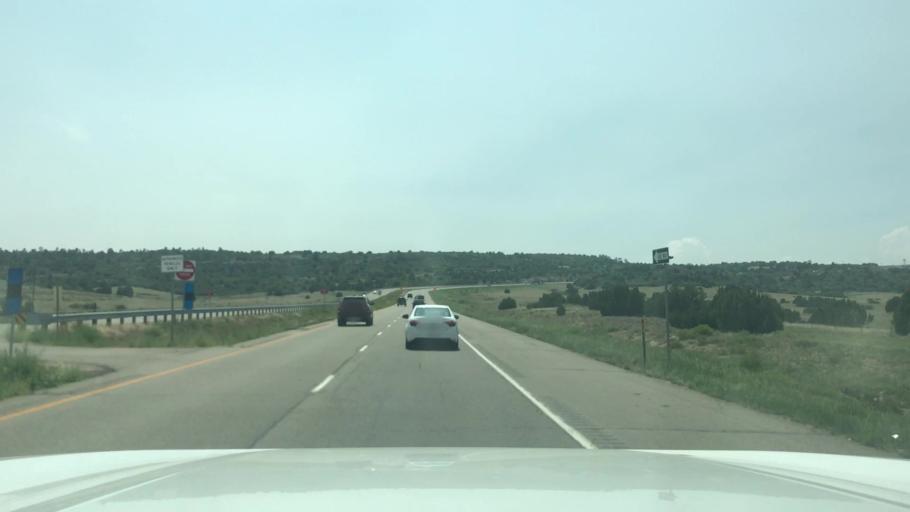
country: US
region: Colorado
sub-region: Pueblo County
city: Colorado City
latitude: 37.9465
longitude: -104.8041
